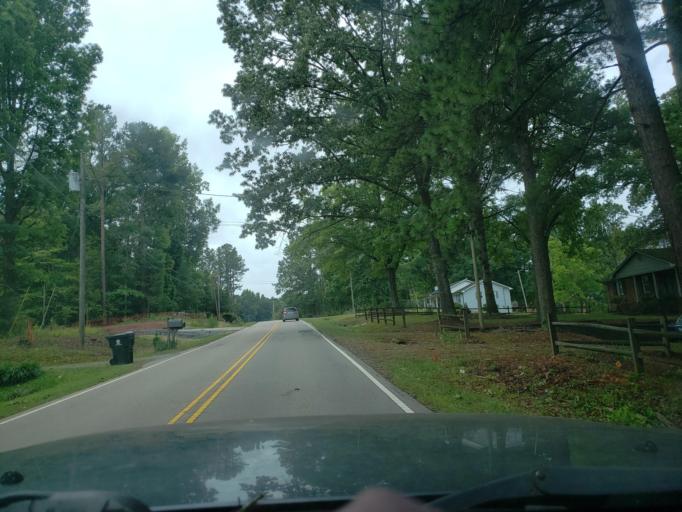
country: US
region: North Carolina
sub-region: Durham County
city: Gorman
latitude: 35.9652
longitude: -78.7828
